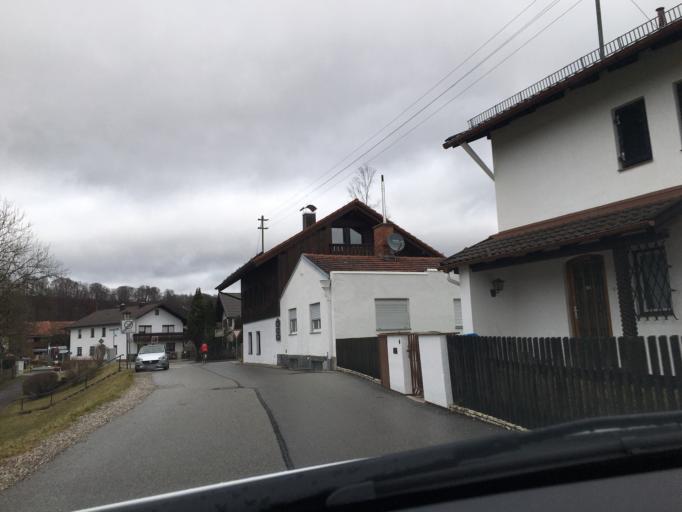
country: DE
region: Bavaria
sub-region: Upper Bavaria
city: Wolfratshausen
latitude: 47.9197
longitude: 11.4275
